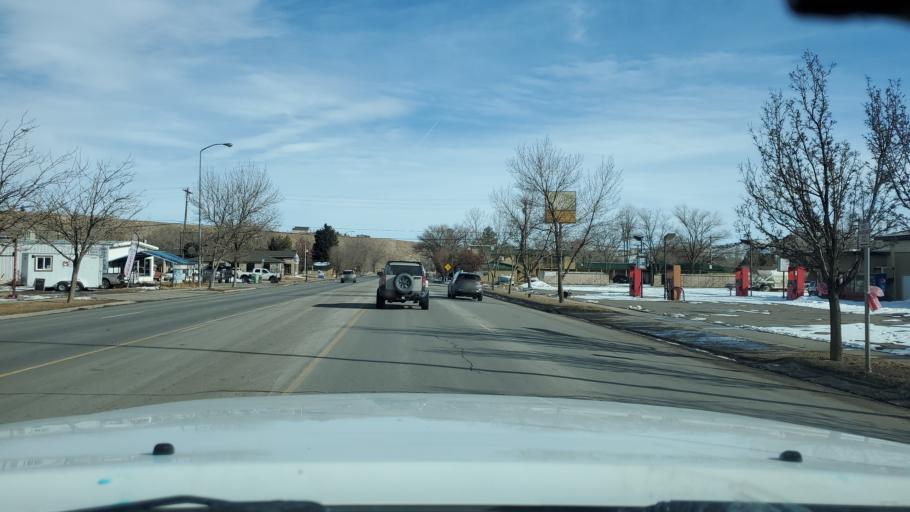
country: US
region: Utah
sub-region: Duchesne County
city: Duchesne
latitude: 40.1634
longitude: -110.3992
